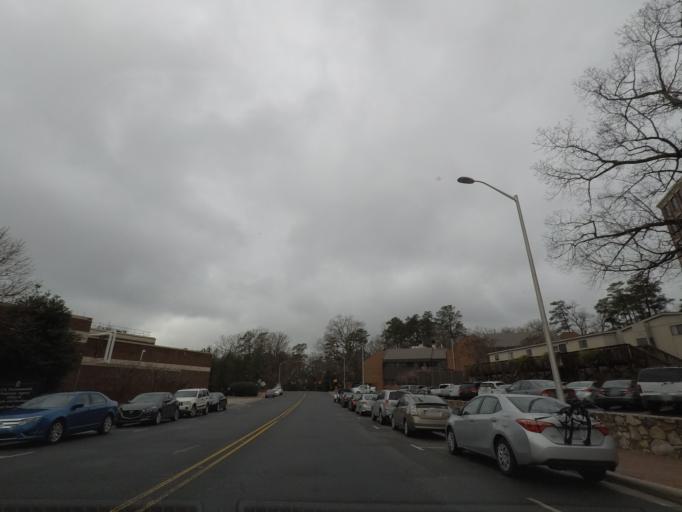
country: US
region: North Carolina
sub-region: Orange County
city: Chapel Hill
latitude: 35.9022
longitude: -79.0549
